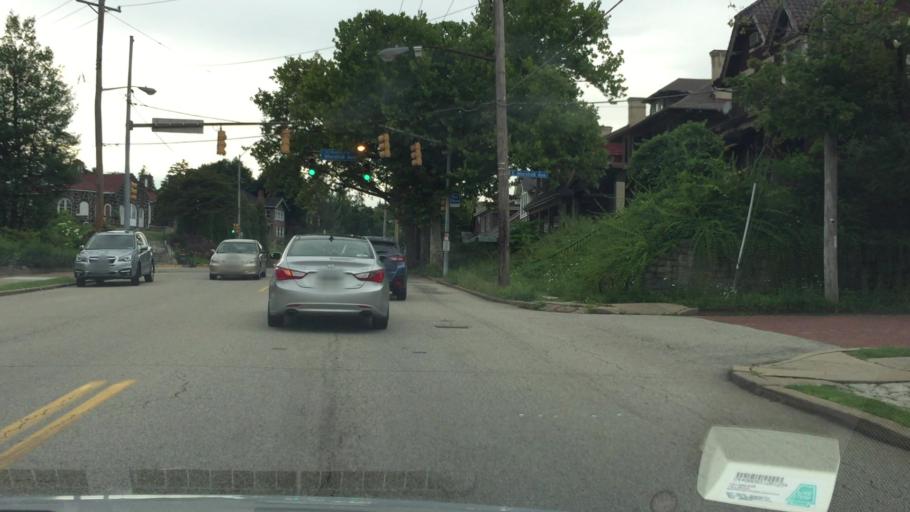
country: US
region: Pennsylvania
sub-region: Allegheny County
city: Millvale
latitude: 40.4747
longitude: -80.0108
